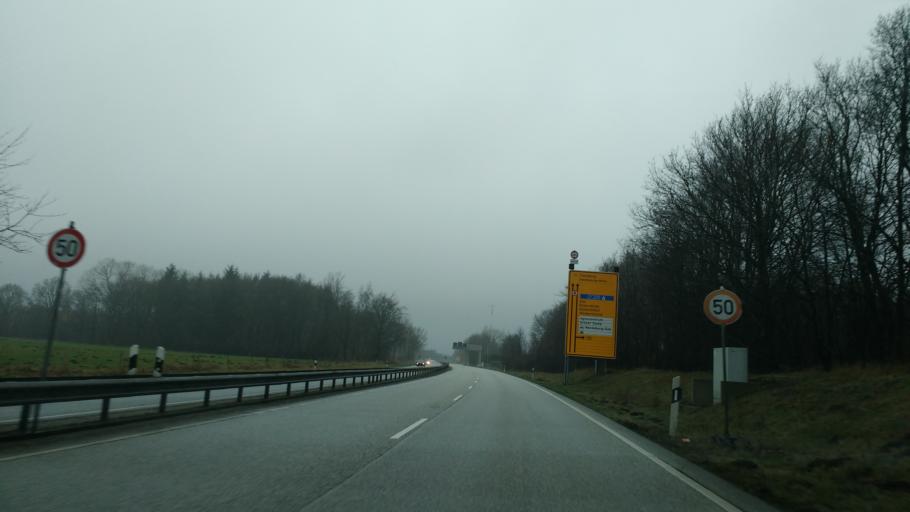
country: DE
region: Schleswig-Holstein
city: Westerronfeld
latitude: 54.2723
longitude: 9.6660
